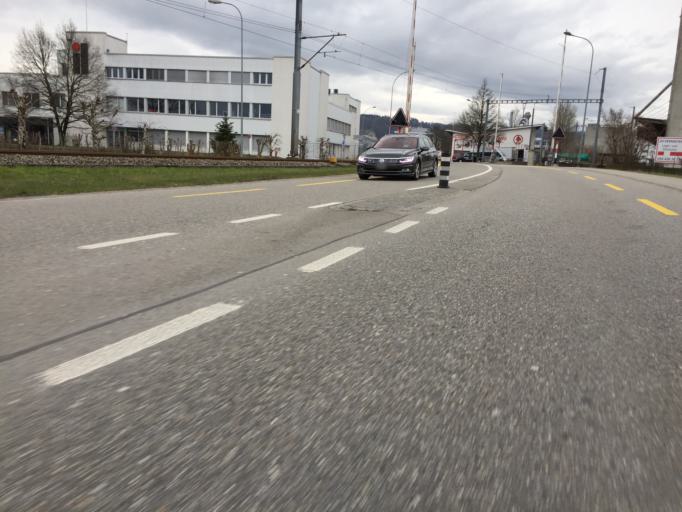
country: CH
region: Bern
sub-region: Emmental District
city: Burgdorf
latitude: 47.0661
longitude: 7.6068
